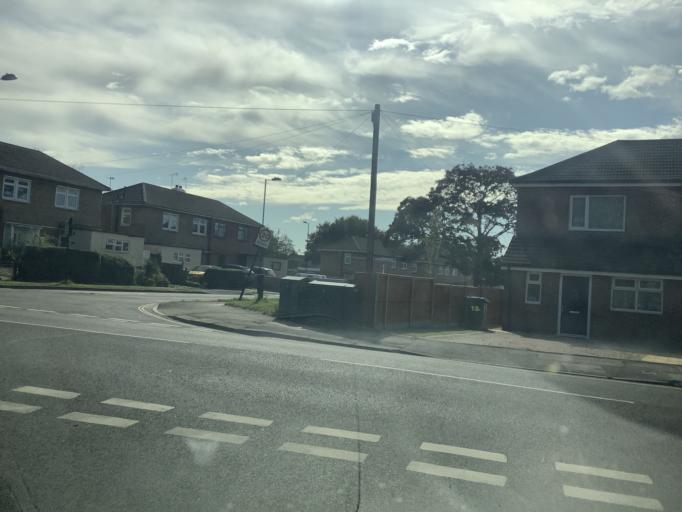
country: GB
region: England
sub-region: Hampshire
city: Marchwood
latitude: 50.9229
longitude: -1.4500
